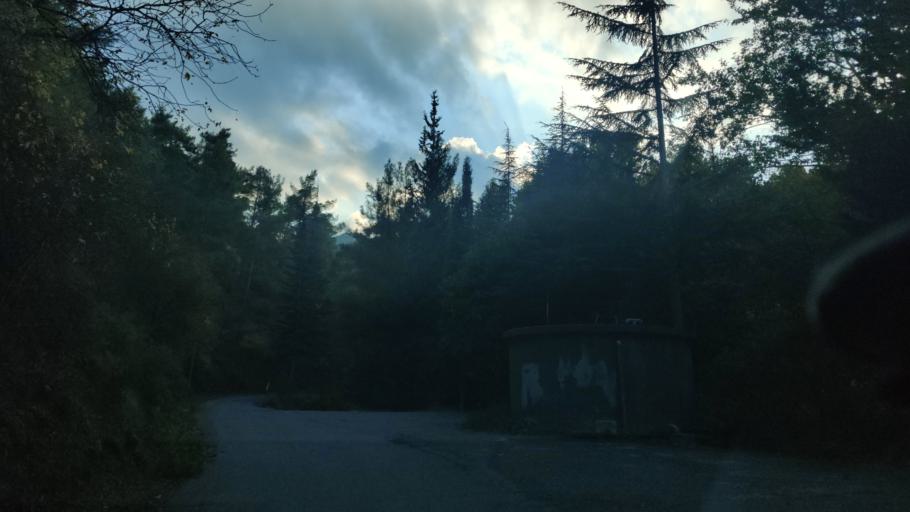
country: CY
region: Lefkosia
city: Lefka
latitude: 35.0671
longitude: 32.7379
